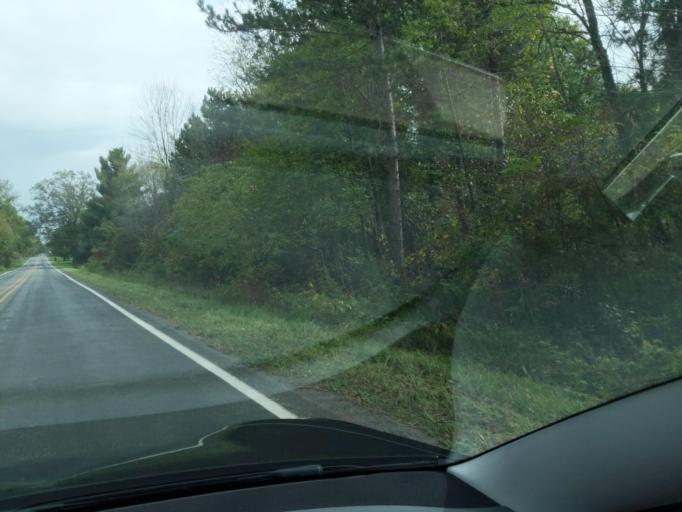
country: US
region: Michigan
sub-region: Eaton County
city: Eaton Rapids
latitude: 42.4657
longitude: -84.5912
